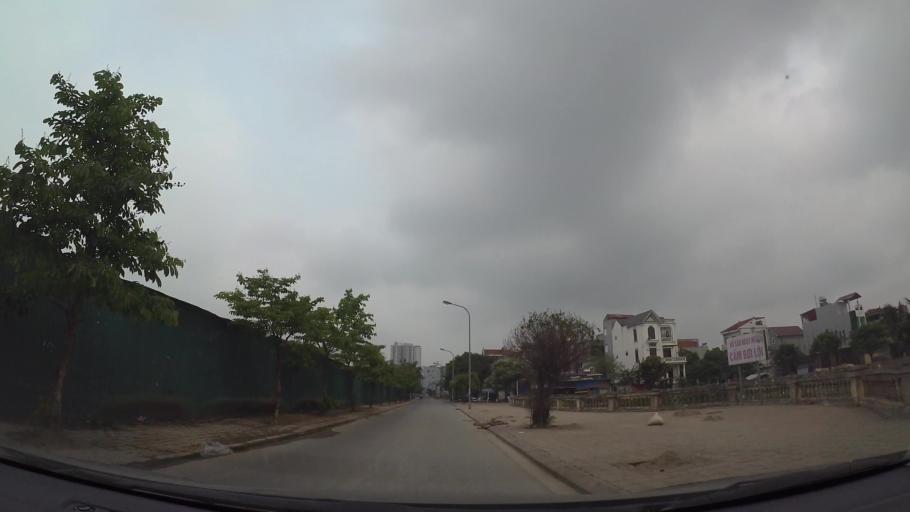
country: VN
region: Ha Noi
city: Trau Quy
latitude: 21.0370
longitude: 105.9328
